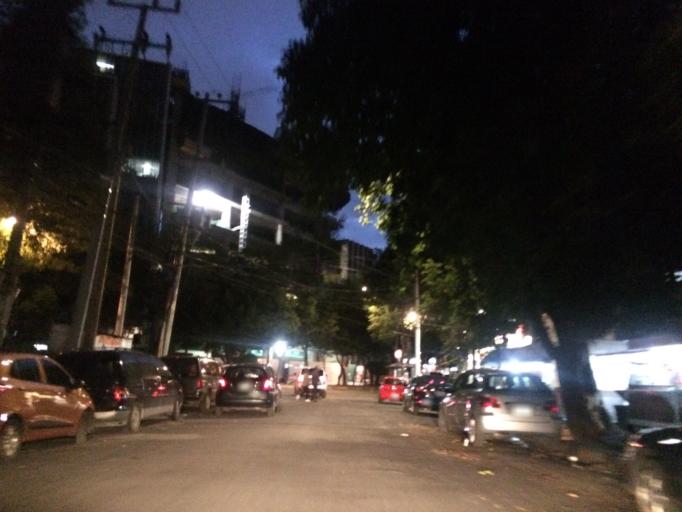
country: MX
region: Mexico City
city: Benito Juarez
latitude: 19.3969
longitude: -99.1711
